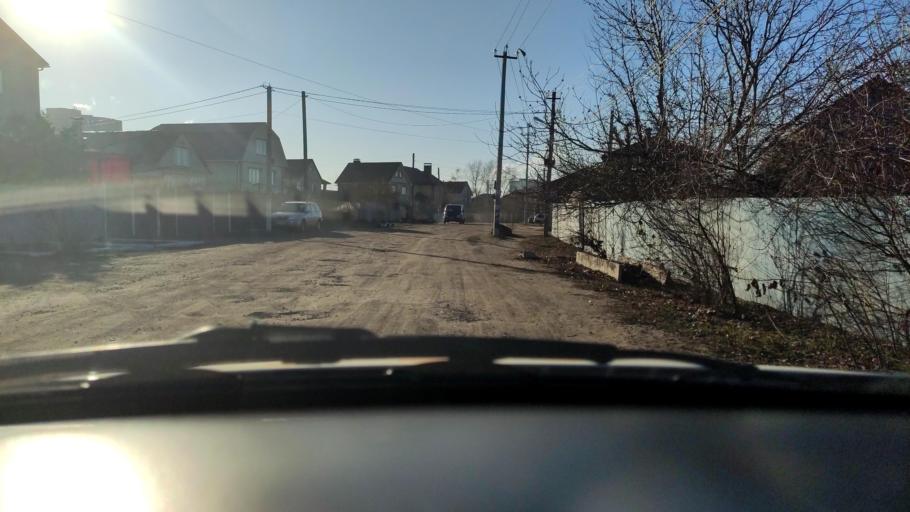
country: RU
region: Voronezj
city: Podgornoye
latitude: 51.7276
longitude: 39.1578
